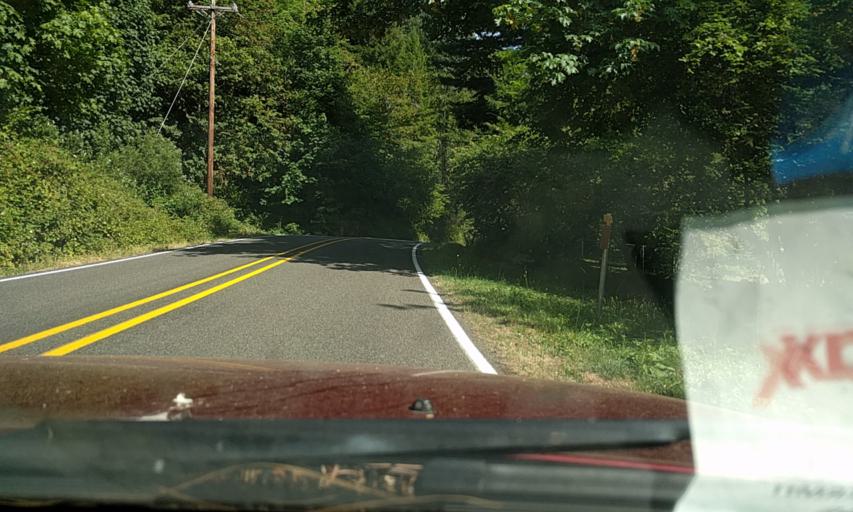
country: US
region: Oregon
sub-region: Lane County
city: Florence
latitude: 44.0415
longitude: -123.8657
